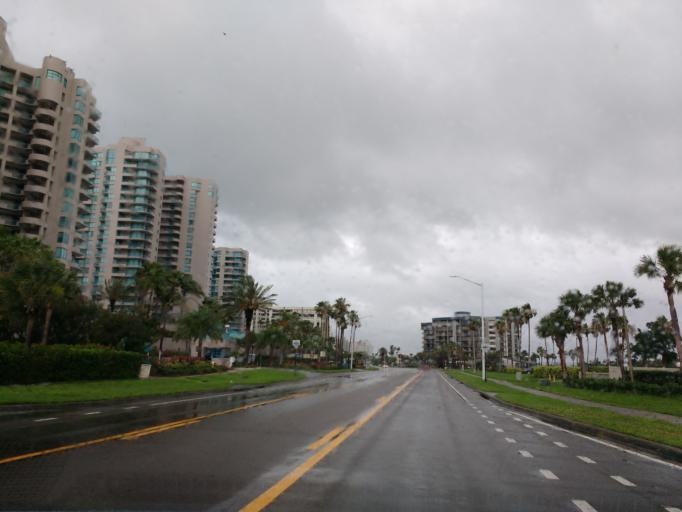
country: US
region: Florida
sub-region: Pinellas County
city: Belleair Beach
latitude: 27.9403
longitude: -82.8374
